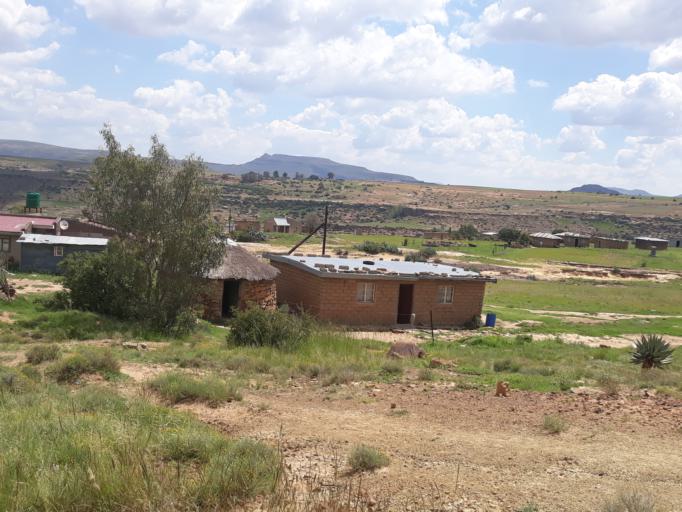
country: LS
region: Quthing
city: Quthing
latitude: -30.3426
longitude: 27.5304
